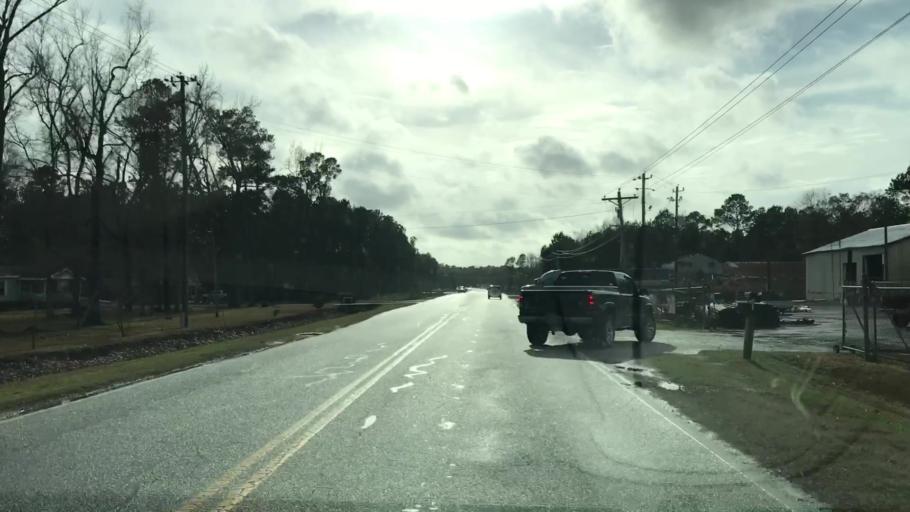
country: US
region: South Carolina
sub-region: Williamsburg County
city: Andrews
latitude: 33.4471
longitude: -79.5866
